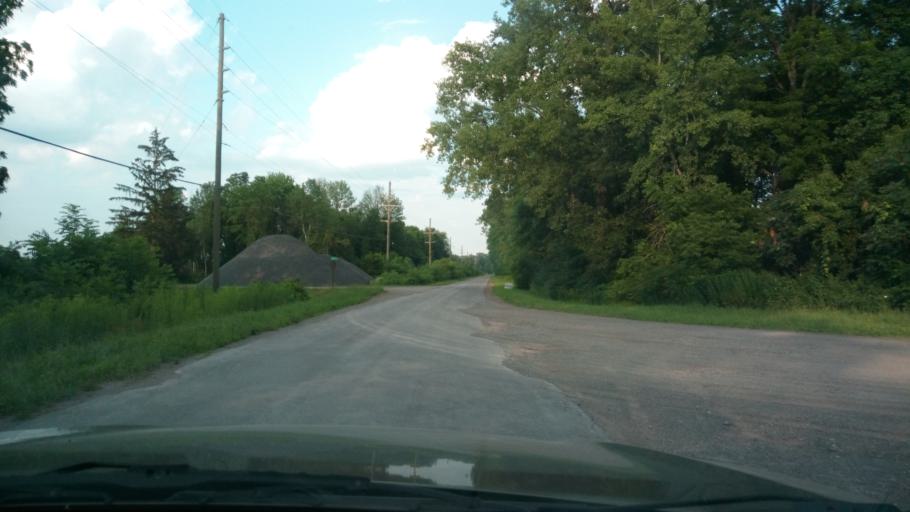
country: US
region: New York
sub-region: Wayne County
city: Clyde
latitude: 43.0880
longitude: -76.9089
